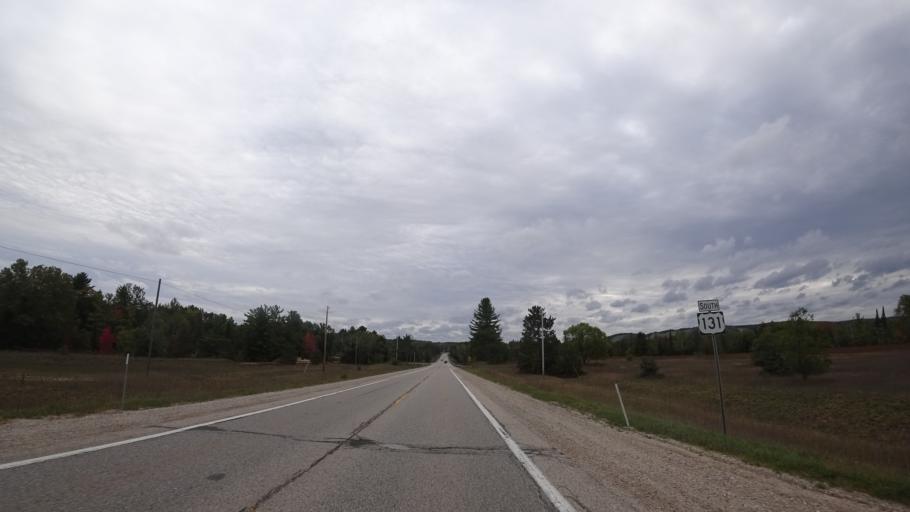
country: US
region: Michigan
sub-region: Charlevoix County
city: Boyne City
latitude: 45.1848
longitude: -84.9147
